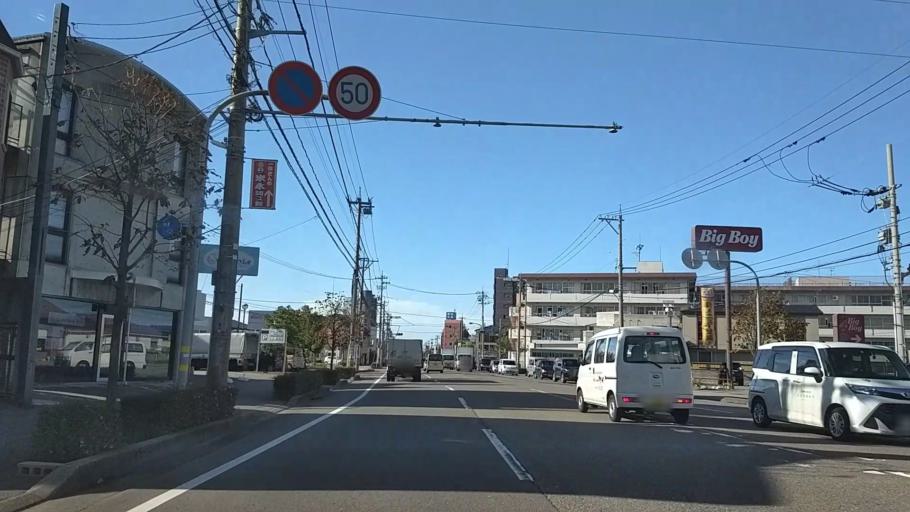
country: JP
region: Ishikawa
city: Kanazawa-shi
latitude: 36.5873
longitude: 136.6479
